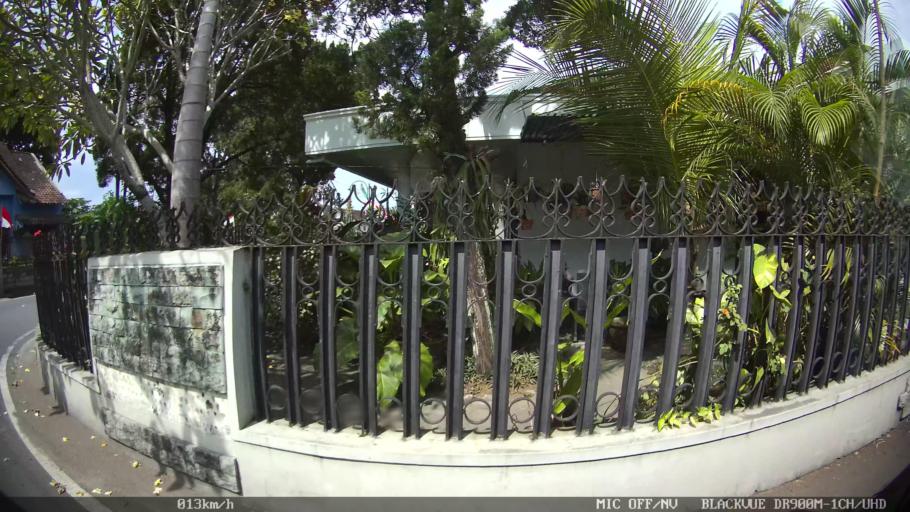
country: ID
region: Daerah Istimewa Yogyakarta
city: Gamping Lor
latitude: -7.8023
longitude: 110.3279
